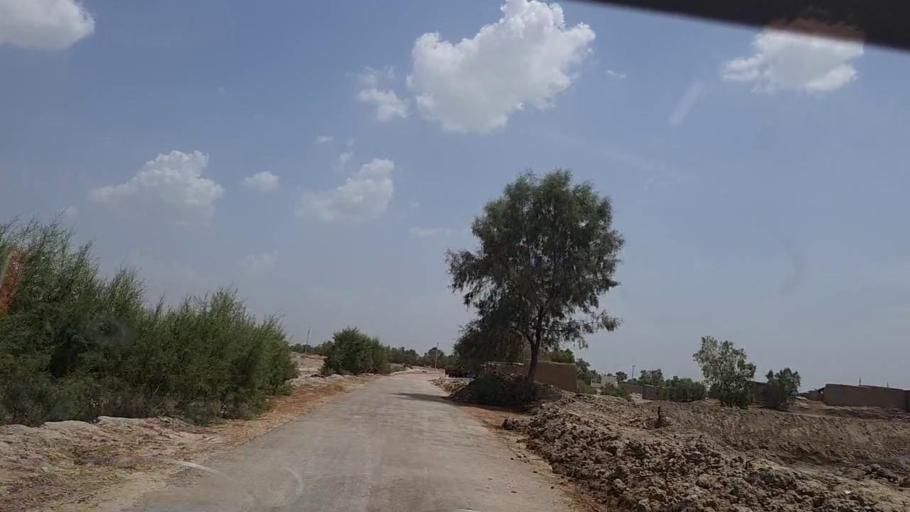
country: PK
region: Sindh
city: Bhan
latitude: 26.5118
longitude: 67.6405
